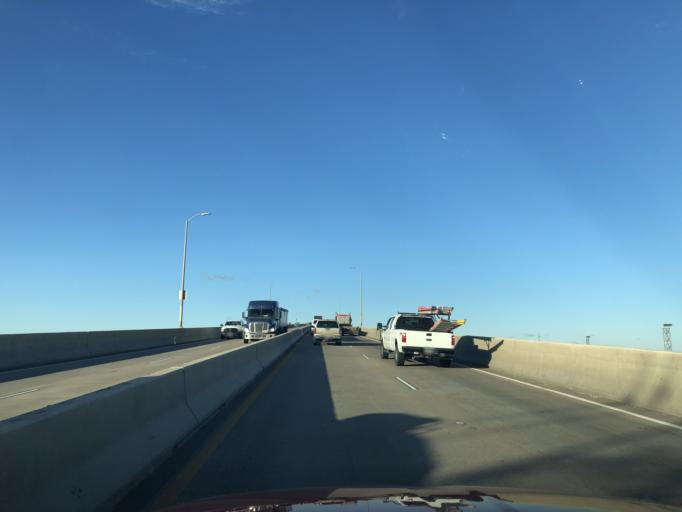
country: US
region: Texas
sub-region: Harris County
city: Deer Park
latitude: 29.7276
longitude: -95.1471
